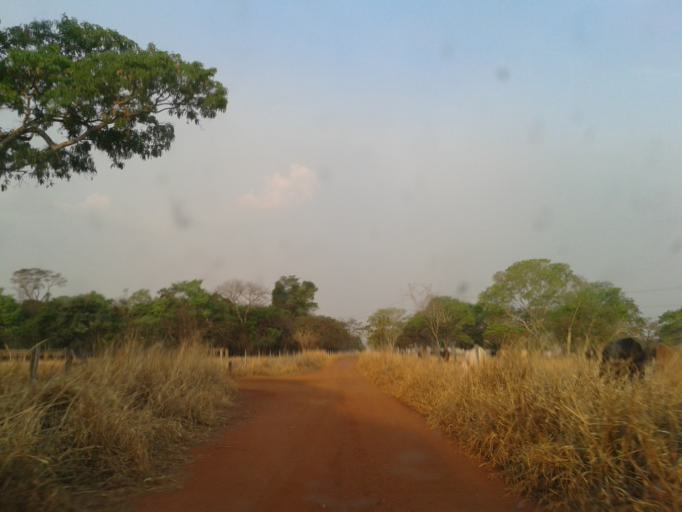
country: BR
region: Minas Gerais
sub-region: Capinopolis
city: Capinopolis
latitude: -18.8066
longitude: -49.7443
